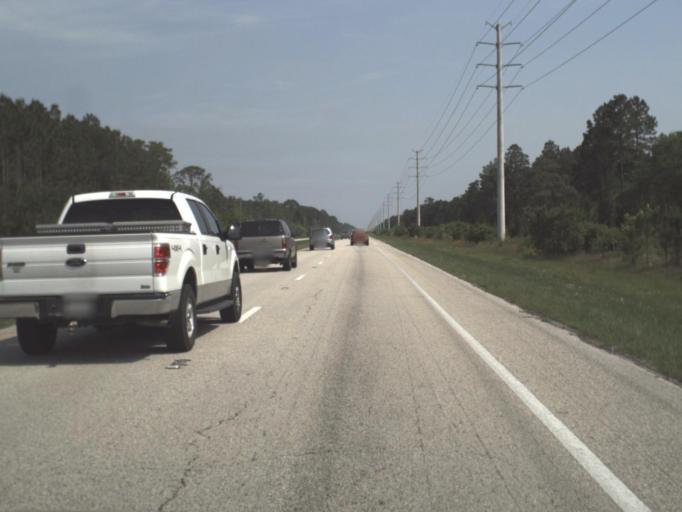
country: US
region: Florida
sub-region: Saint Johns County
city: Palm Valley
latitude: 30.0374
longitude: -81.4147
